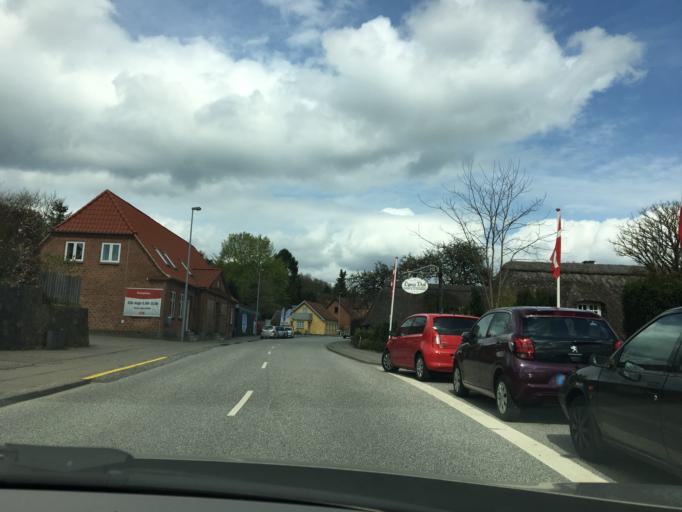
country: DK
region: Central Jutland
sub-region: Skanderborg Kommune
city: Ry
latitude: 56.0745
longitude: 9.6984
